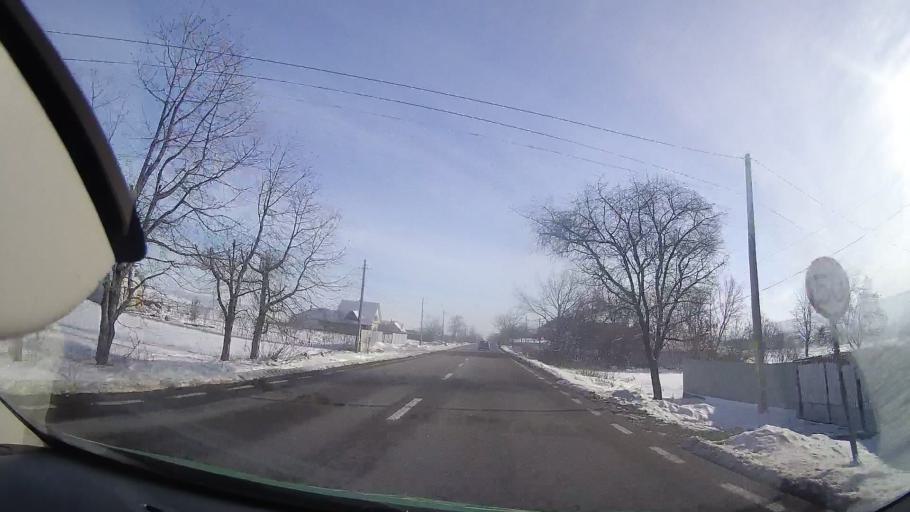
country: RO
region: Neamt
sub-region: Comuna Negresti
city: Negresti
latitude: 47.0618
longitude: 26.3822
